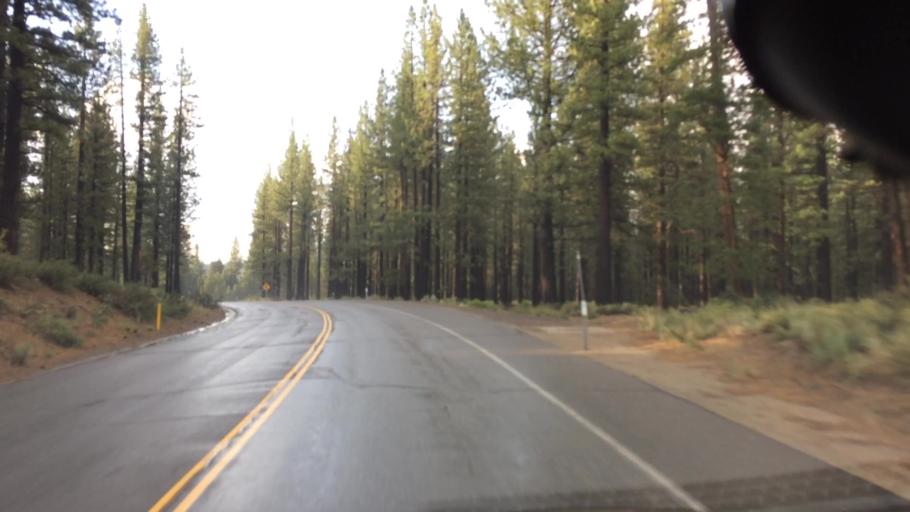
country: US
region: California
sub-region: El Dorado County
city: South Lake Tahoe
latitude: 38.9006
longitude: -119.9697
